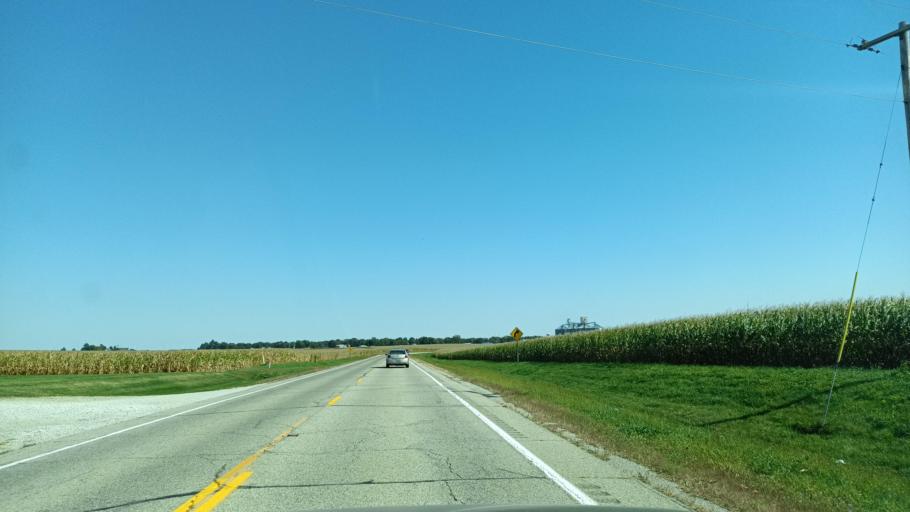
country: US
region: Illinois
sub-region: McLean County
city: Le Roy
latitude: 40.3580
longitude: -88.7863
